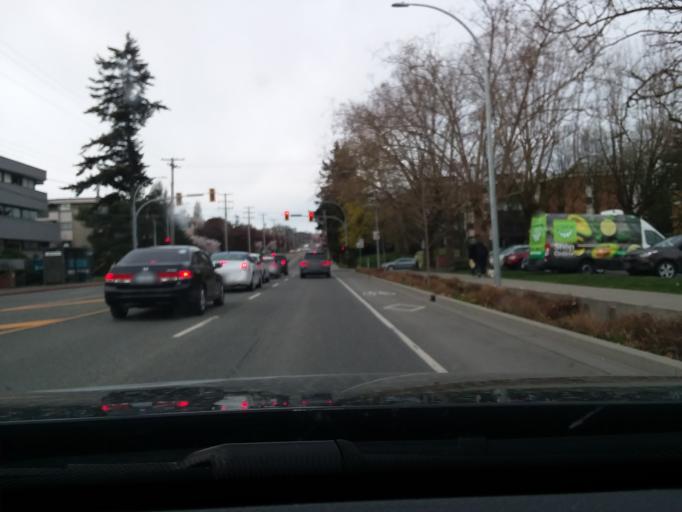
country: CA
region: British Columbia
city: Victoria
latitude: 48.4441
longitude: -123.3375
